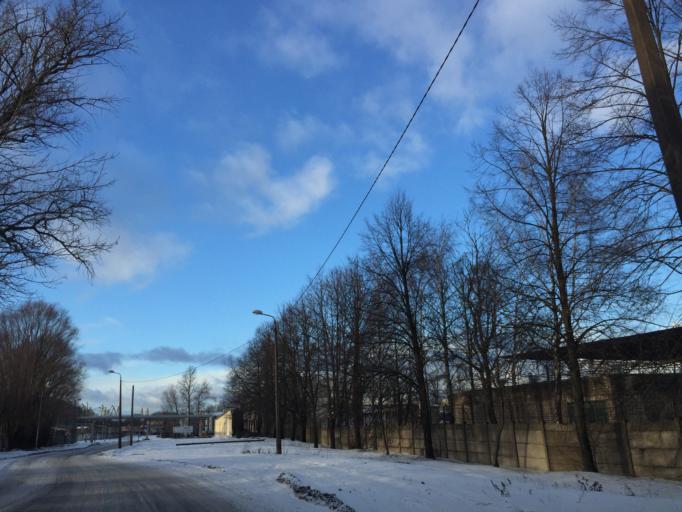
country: LV
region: Riga
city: Riga
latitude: 56.9805
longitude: 24.1133
